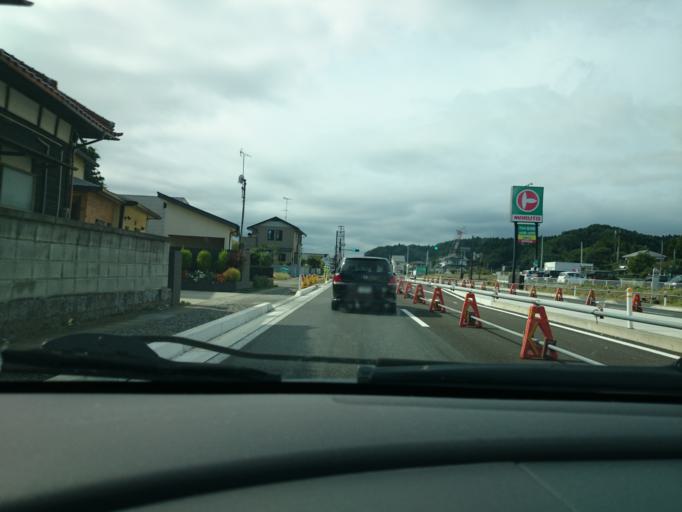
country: JP
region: Fukushima
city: Iwaki
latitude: 36.9803
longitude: 140.8853
